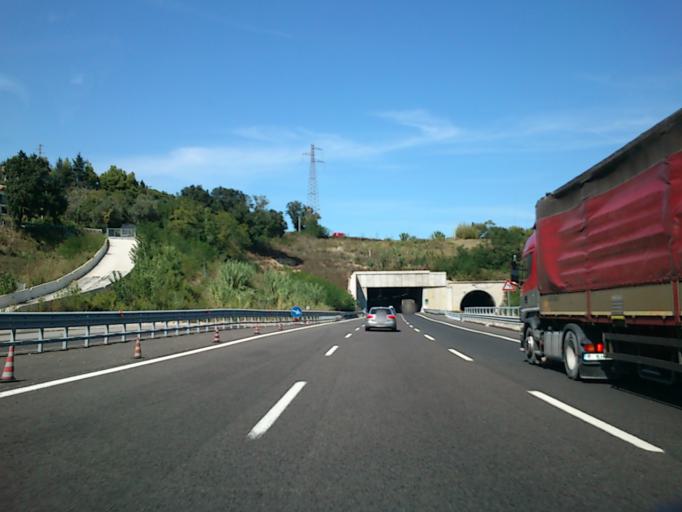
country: IT
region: The Marches
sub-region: Provincia di Pesaro e Urbino
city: Fenile
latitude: 43.8612
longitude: 12.9357
